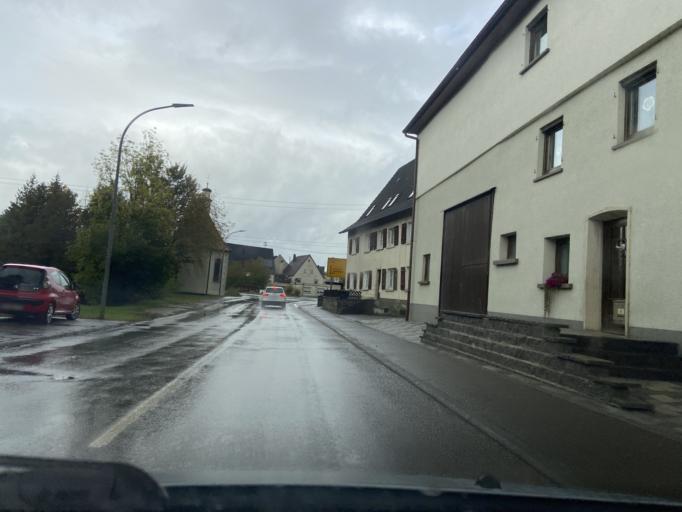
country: DE
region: Baden-Wuerttemberg
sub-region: Tuebingen Region
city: Bingen
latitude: 48.1038
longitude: 9.2894
